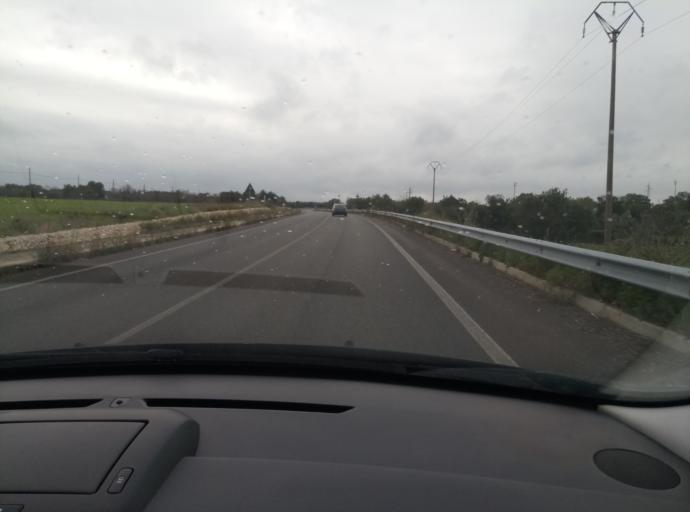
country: IT
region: Apulia
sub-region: Provincia di Bari
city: Acquaviva delle Fonti
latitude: 40.8791
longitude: 16.8102
